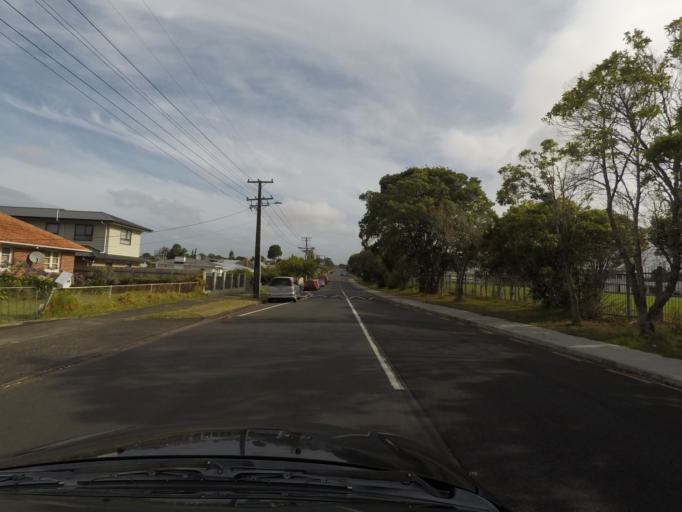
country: NZ
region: Auckland
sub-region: Auckland
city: Waitakere
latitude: -36.8984
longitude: 174.6675
